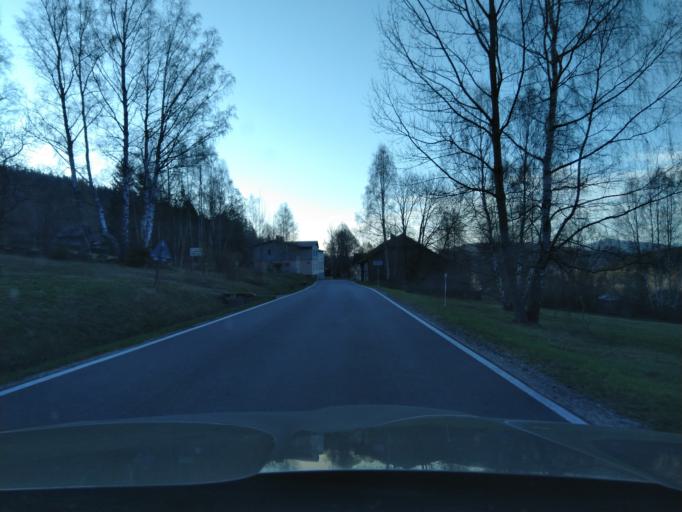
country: CZ
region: Jihocesky
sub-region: Okres Prachatice
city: Vimperk
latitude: 48.9496
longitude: 13.7855
